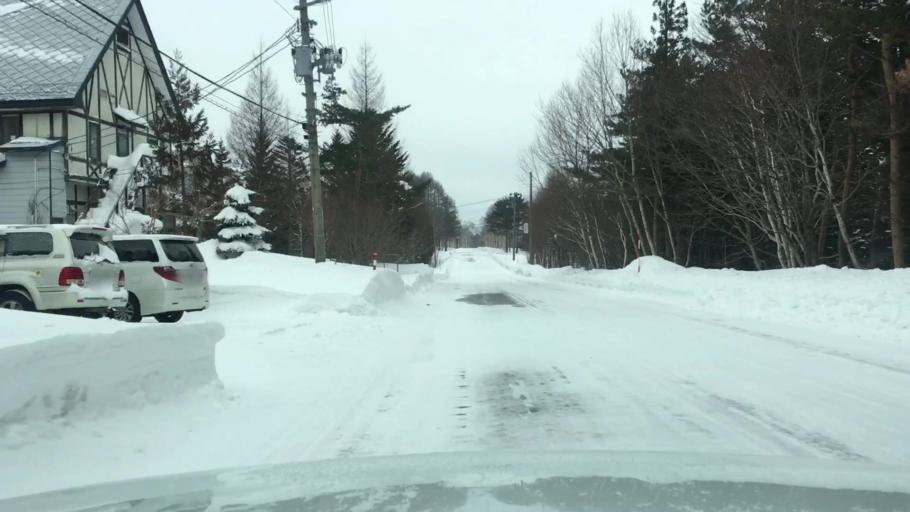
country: JP
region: Akita
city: Hanawa
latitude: 40.0041
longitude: 140.9811
